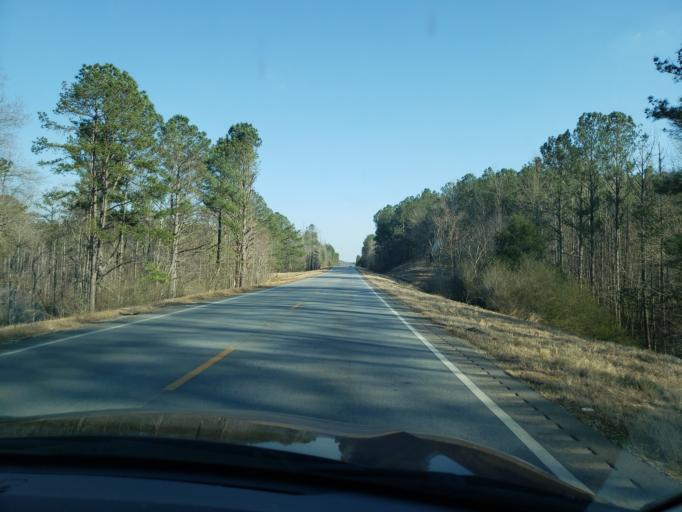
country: US
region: Alabama
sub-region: Randolph County
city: Wedowee
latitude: 33.4102
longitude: -85.5417
